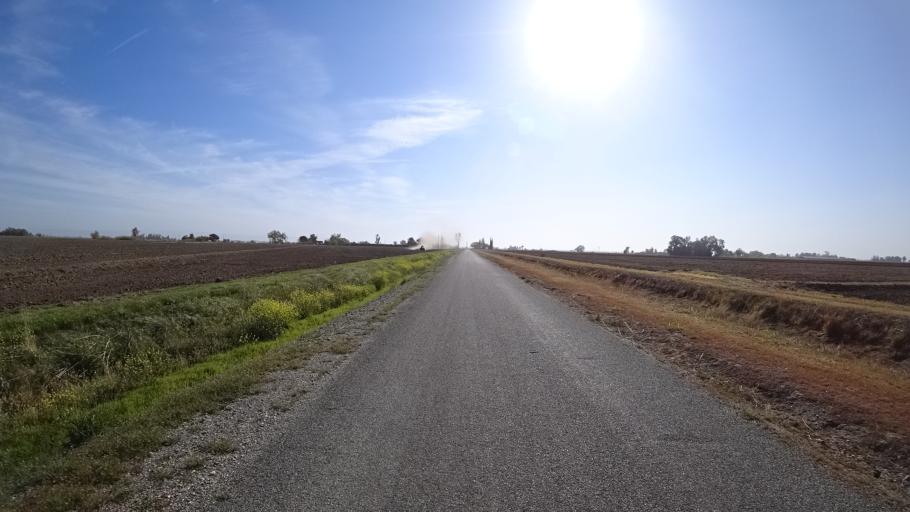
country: US
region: California
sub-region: Glenn County
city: Willows
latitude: 39.5604
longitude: -122.1137
